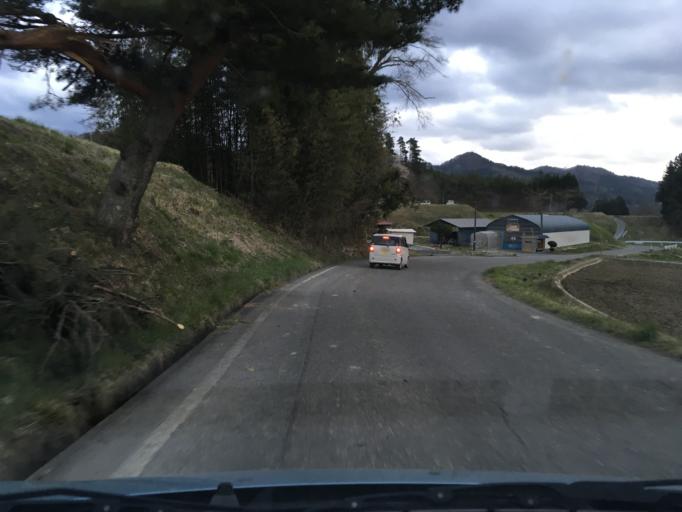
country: JP
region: Iwate
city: Ichinoseki
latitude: 38.9685
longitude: 141.2163
